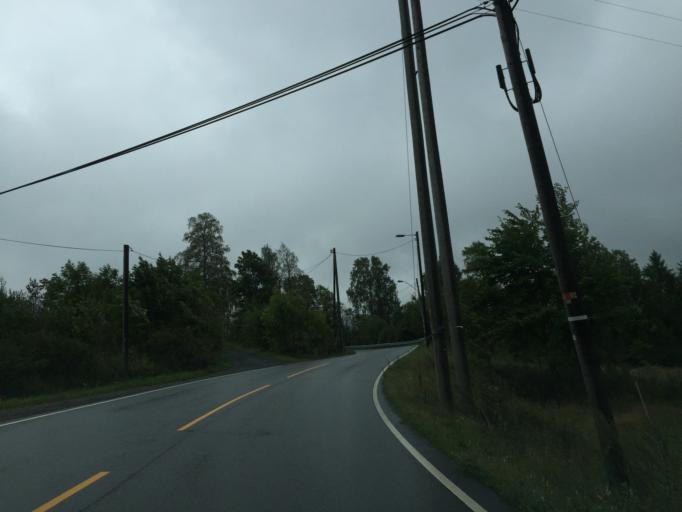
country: NO
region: Akershus
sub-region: Baerum
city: Lysaker
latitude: 60.0053
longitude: 10.6196
